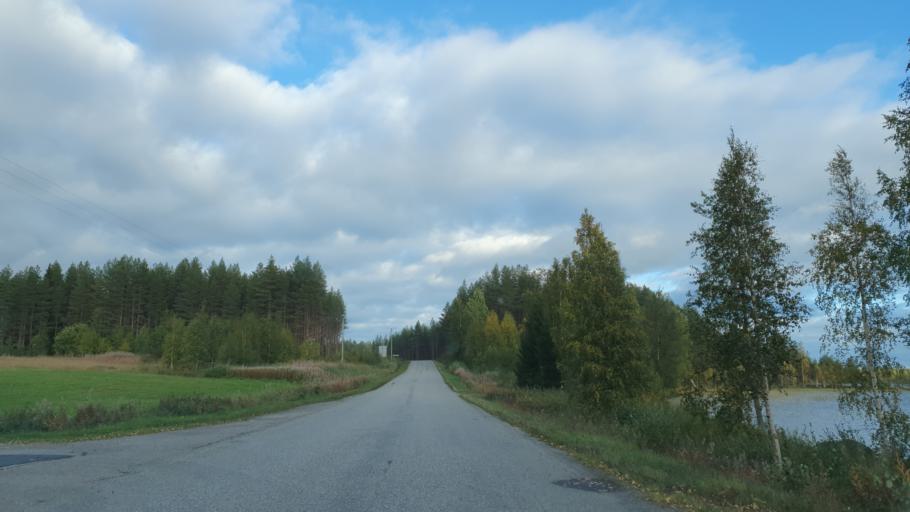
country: FI
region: Kainuu
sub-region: Kehys-Kainuu
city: Kuhmo
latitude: 63.9306
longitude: 29.9755
